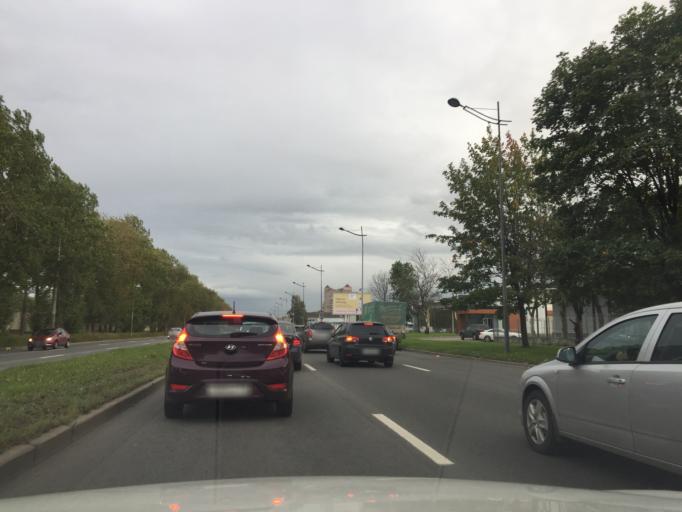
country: RU
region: St.-Petersburg
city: Kupchino
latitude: 59.8715
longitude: 30.3542
